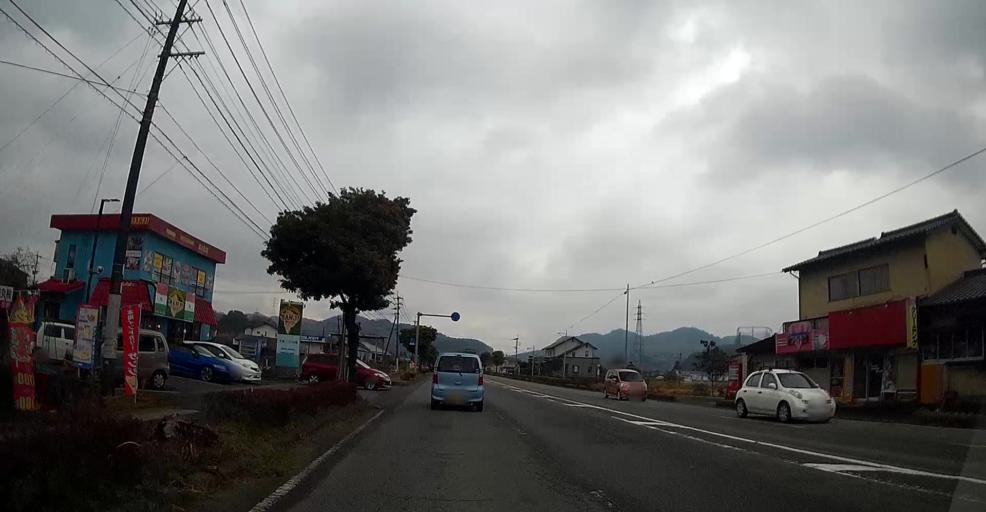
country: JP
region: Kumamoto
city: Matsubase
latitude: 32.6498
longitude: 130.7120
